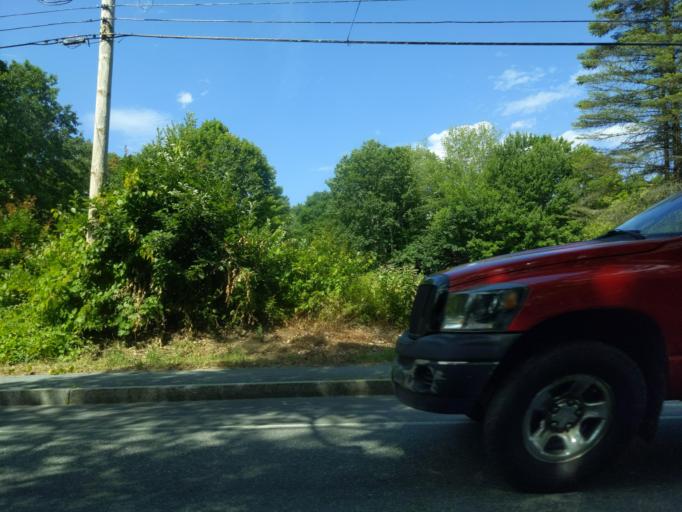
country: US
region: Vermont
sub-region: Windsor County
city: White River Junction
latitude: 43.6378
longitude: -72.3016
